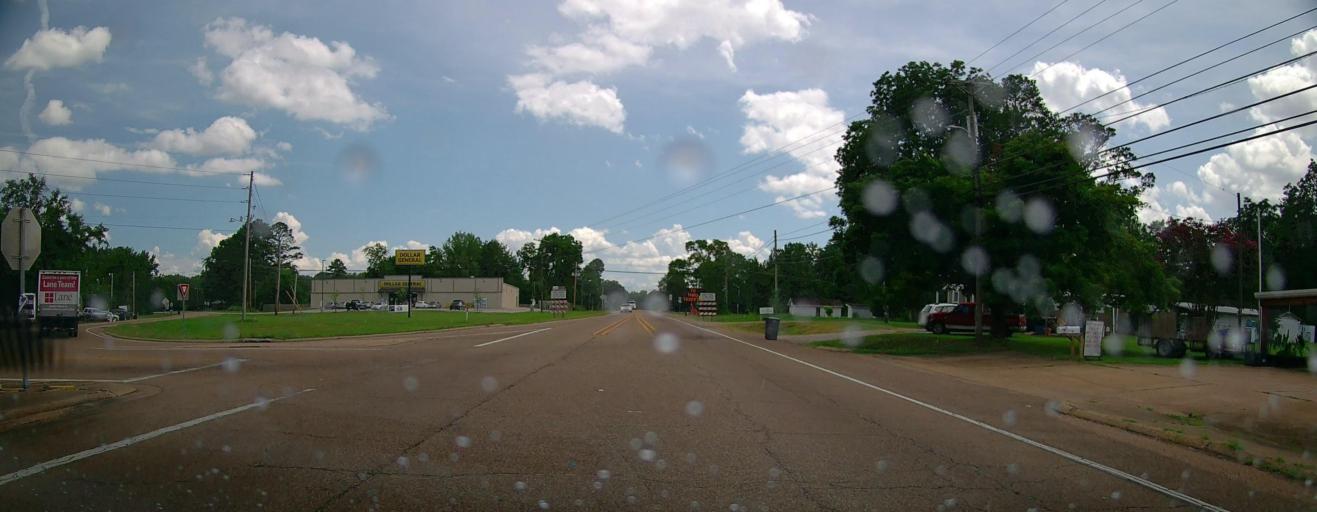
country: US
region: Mississippi
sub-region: Lee County
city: Shannon
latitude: 34.1261
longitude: -88.7193
